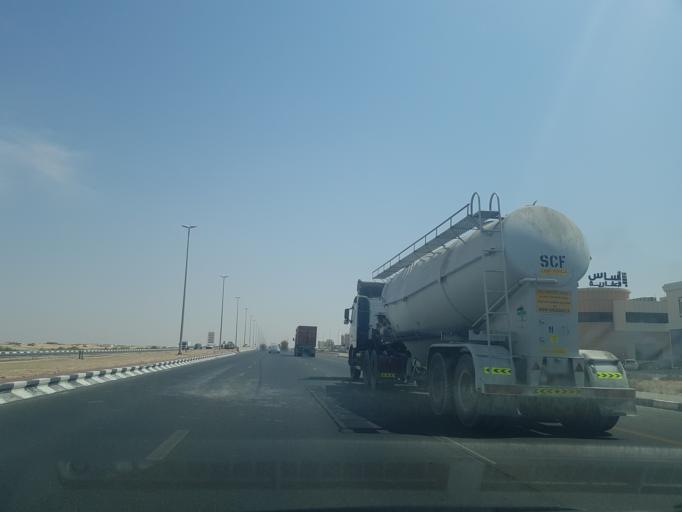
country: AE
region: Ash Shariqah
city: Sharjah
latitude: 25.2587
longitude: 55.5124
